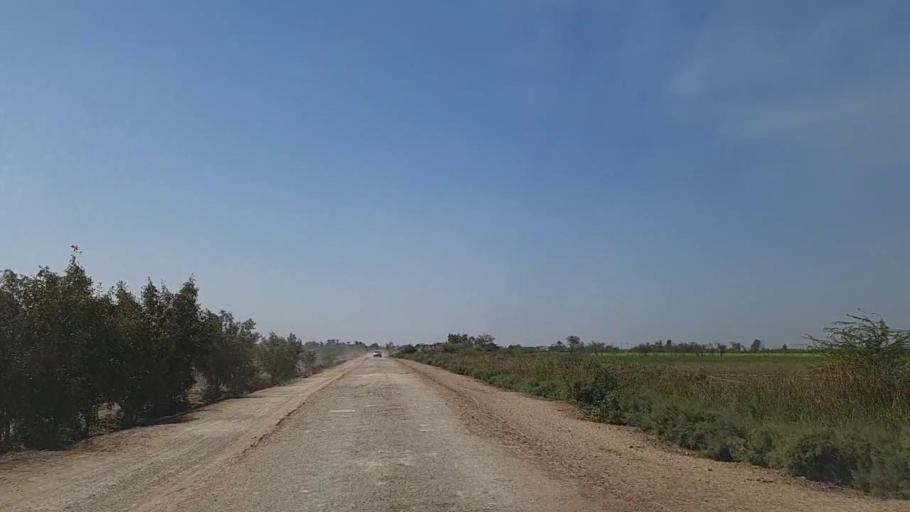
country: PK
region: Sindh
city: Pithoro
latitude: 25.4088
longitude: 69.3153
